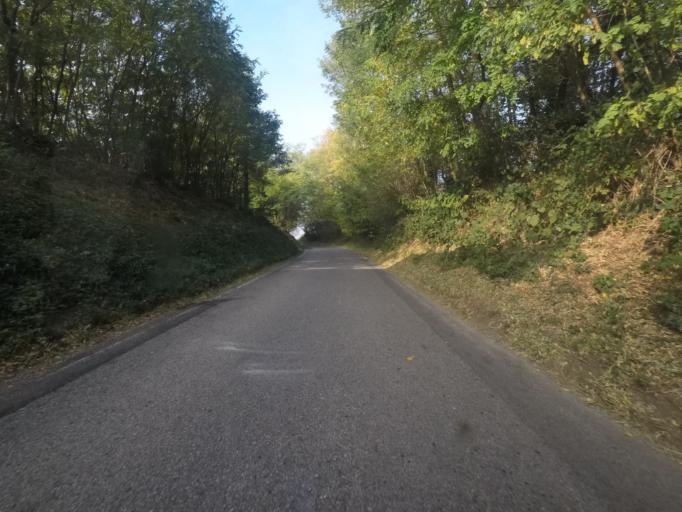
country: IT
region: Lombardy
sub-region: Provincia di Monza e Brianza
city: Bellusco
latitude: 45.6264
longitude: 9.4077
